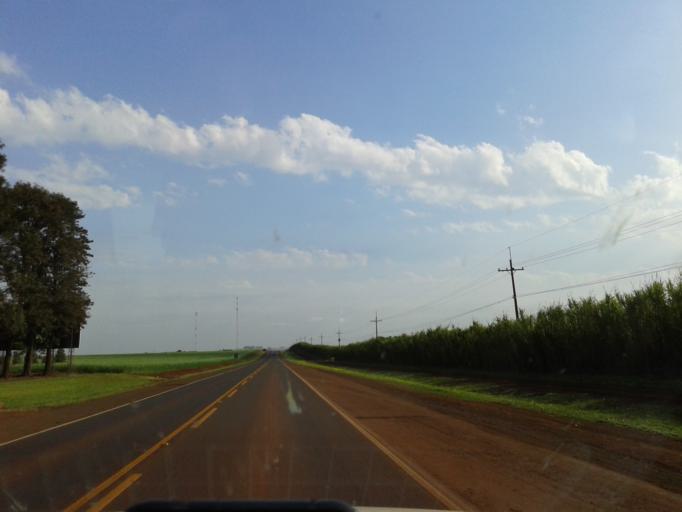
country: PY
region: Itapua
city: Pirapo
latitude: -26.8647
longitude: -55.4541
